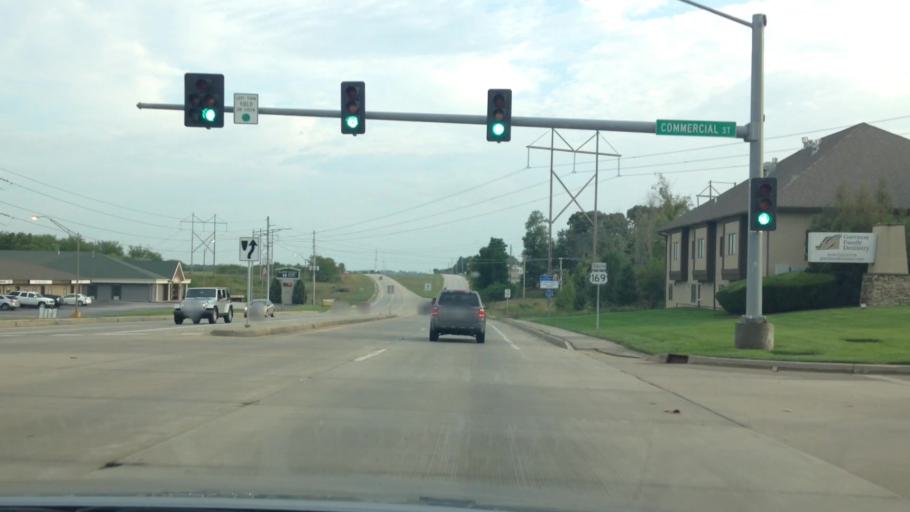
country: US
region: Missouri
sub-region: Clay County
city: Smithville
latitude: 39.3617
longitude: -94.5839
